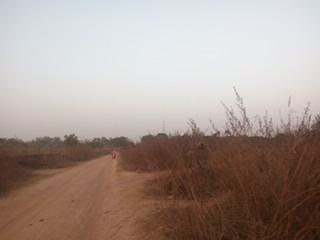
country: BJ
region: Borgou
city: Parakou
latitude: 9.3277
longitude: 2.5960
